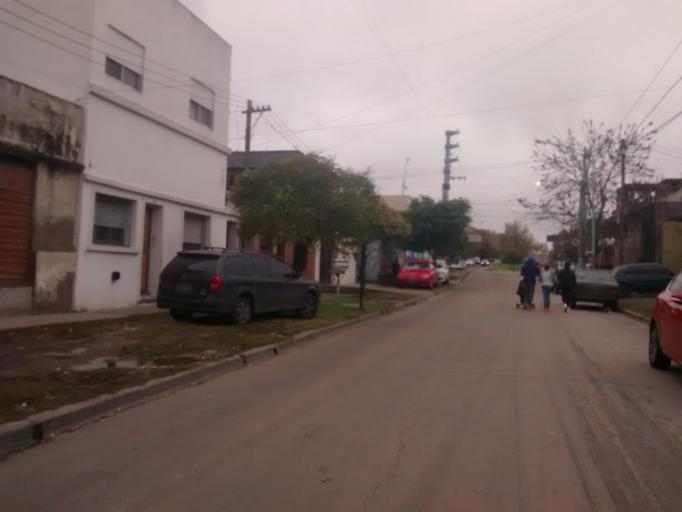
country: AR
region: Buenos Aires
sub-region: Partido de La Plata
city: La Plata
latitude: -34.8916
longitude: -57.9467
